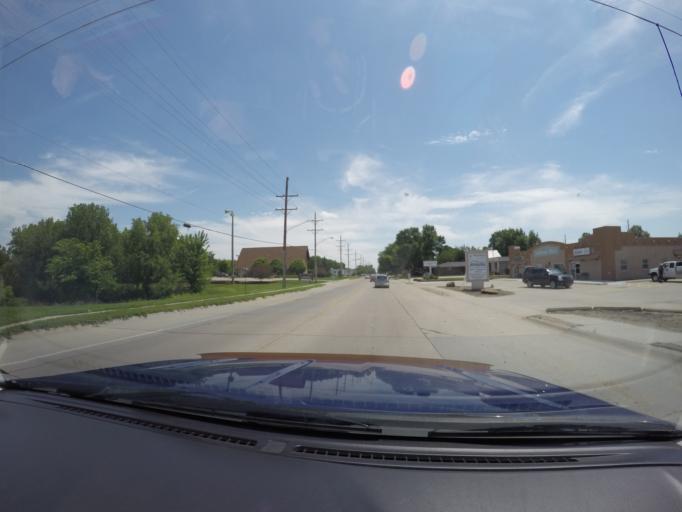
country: US
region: Nebraska
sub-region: Hall County
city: Grand Island
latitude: 40.9024
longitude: -98.3684
